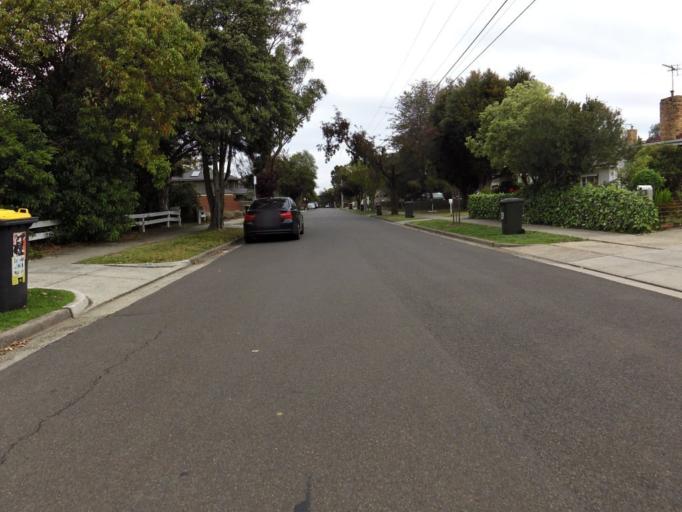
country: AU
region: Victoria
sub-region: Monash
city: Clayton
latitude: -37.9107
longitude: 145.1281
